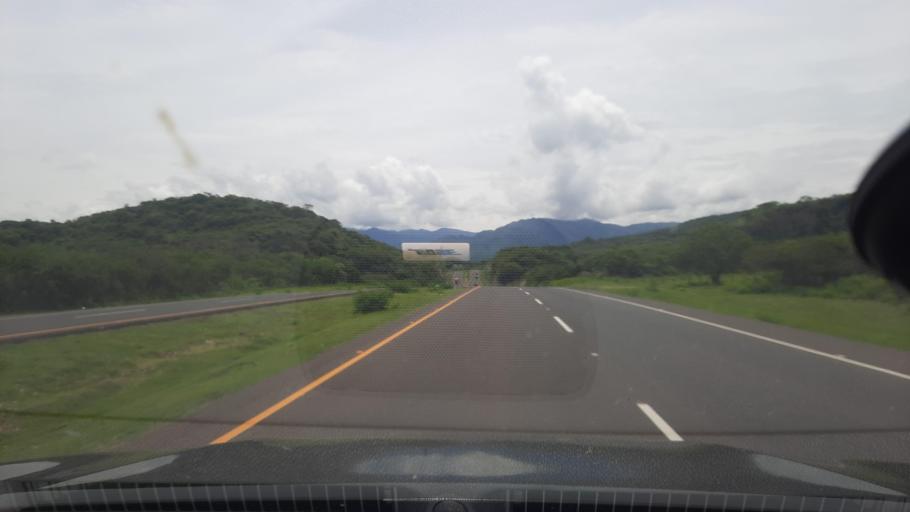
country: HN
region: Valle
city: Aramecina
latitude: 13.6877
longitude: -87.7220
